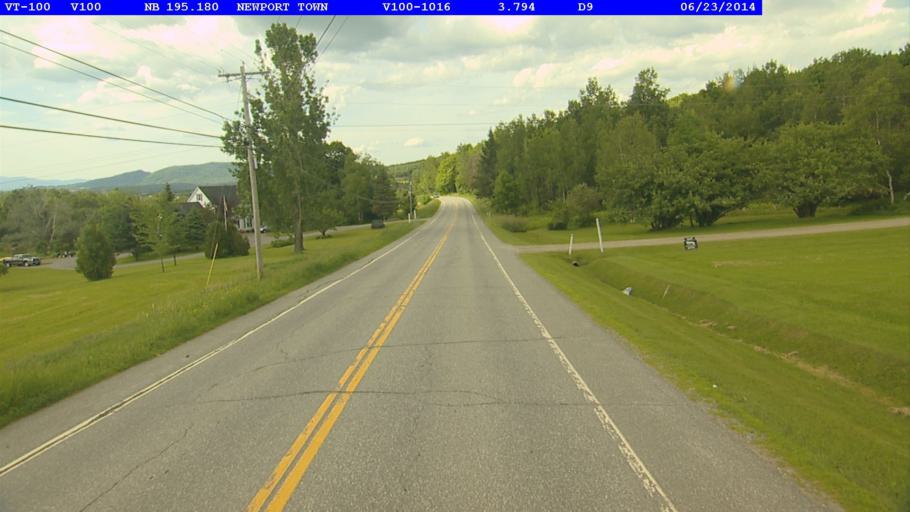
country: US
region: Vermont
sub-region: Orleans County
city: Newport
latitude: 44.9256
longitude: -72.2886
